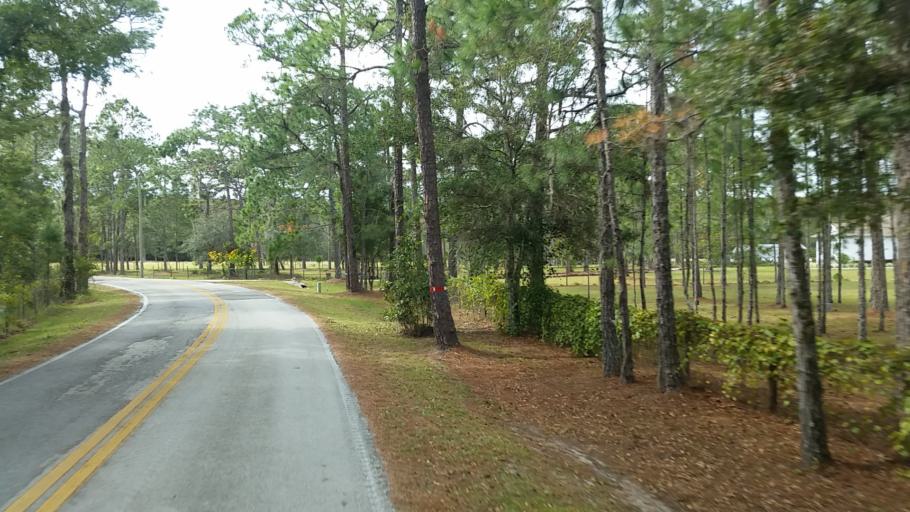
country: US
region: Florida
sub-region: Polk County
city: Polk City
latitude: 28.3248
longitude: -81.8551
